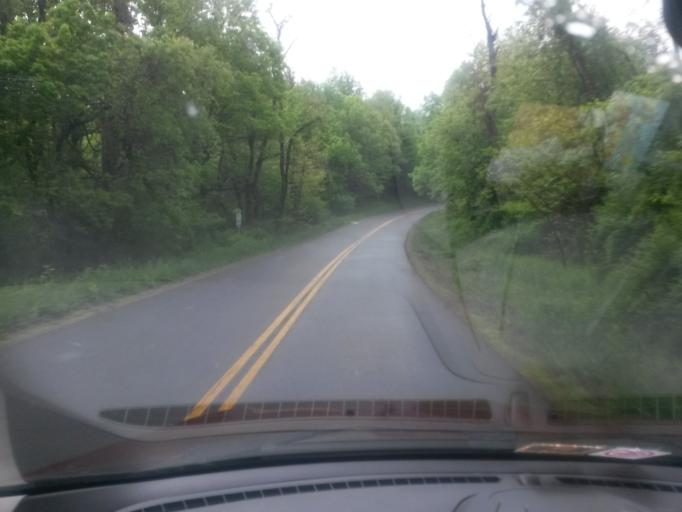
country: US
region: Virginia
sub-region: Floyd County
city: Floyd
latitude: 36.7848
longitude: -80.3853
